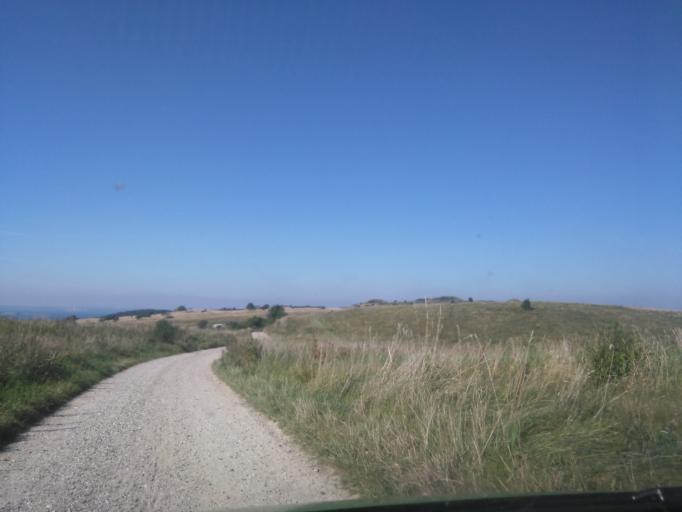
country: DK
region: Central Jutland
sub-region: Syddjurs Kommune
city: Ronde
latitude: 56.1981
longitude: 10.5357
